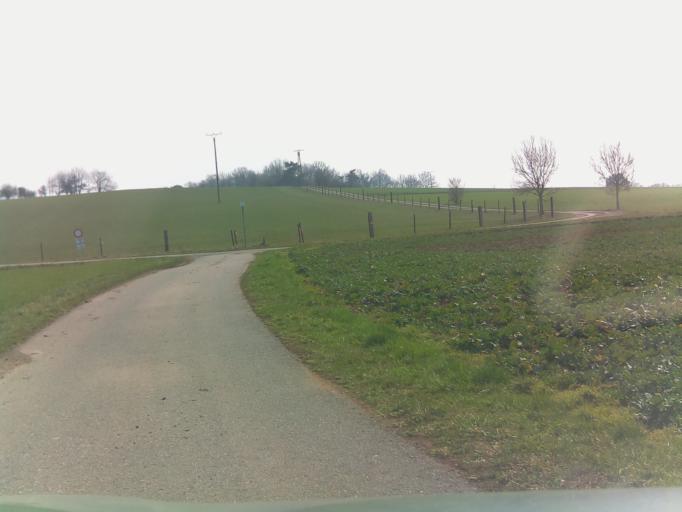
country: DE
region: Rheinland-Pfalz
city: Ruschberg
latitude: 49.6033
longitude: 7.2857
